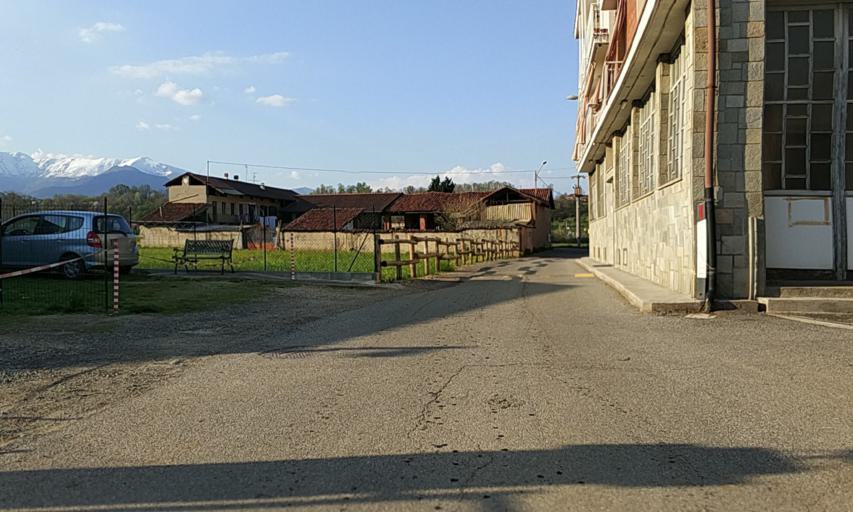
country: IT
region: Piedmont
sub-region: Provincia di Torino
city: Nole
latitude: 45.2480
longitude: 7.5857
